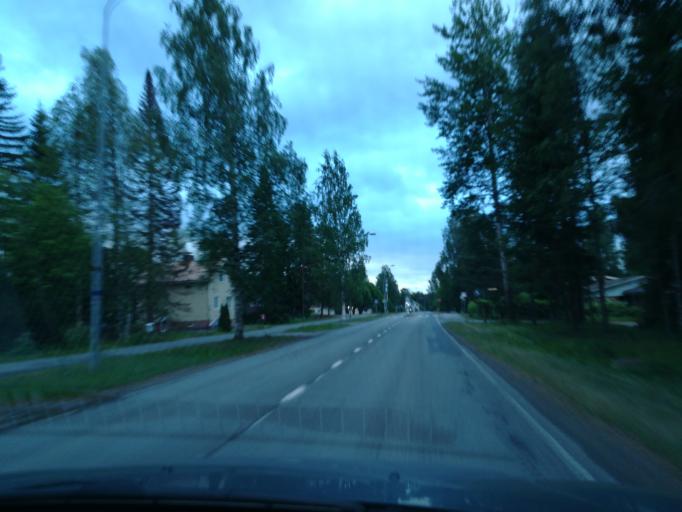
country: FI
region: Southern Savonia
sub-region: Mikkeli
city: Ristiina
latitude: 61.5084
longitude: 27.2528
